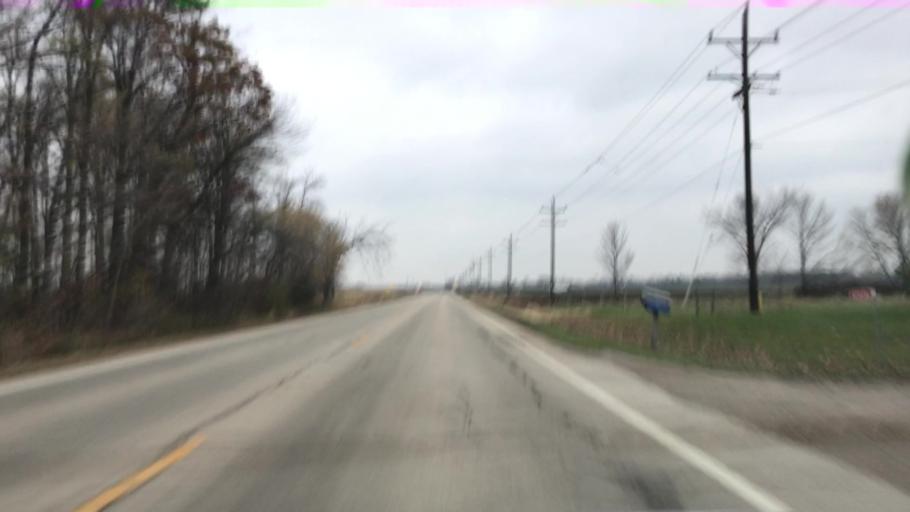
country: US
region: Wisconsin
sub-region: Outagamie County
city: Seymour
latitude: 44.4935
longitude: -88.2912
